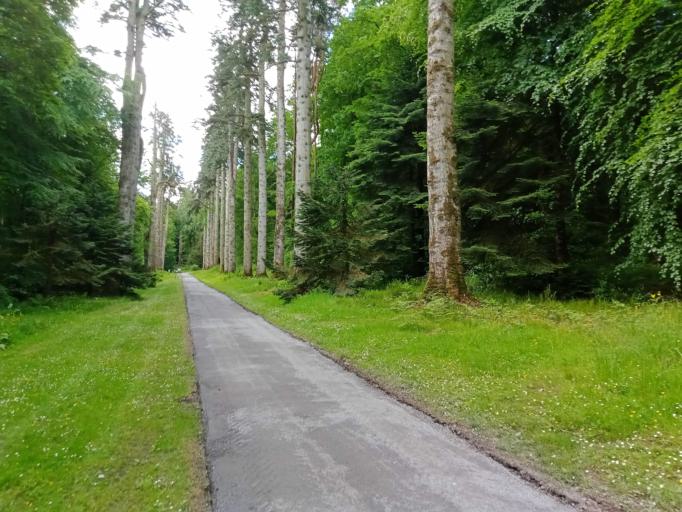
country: IE
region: Leinster
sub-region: Kilkenny
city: Thomastown
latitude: 52.4727
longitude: -7.0578
